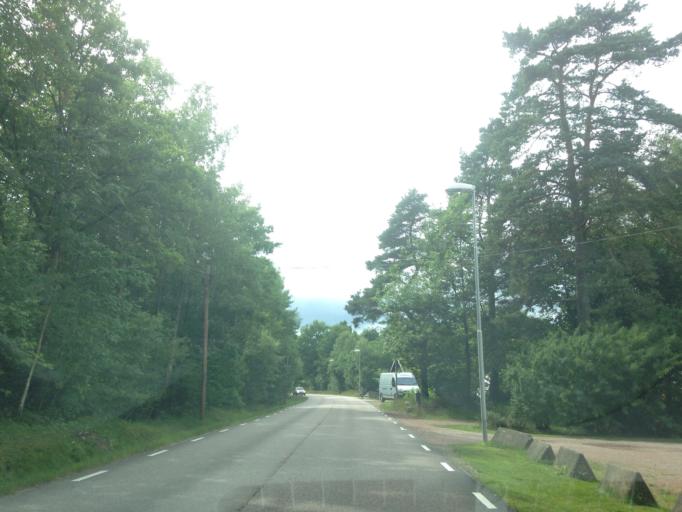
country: SE
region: Vaestra Goetaland
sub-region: Ale Kommun
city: Surte
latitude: 57.7801
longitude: 11.9632
